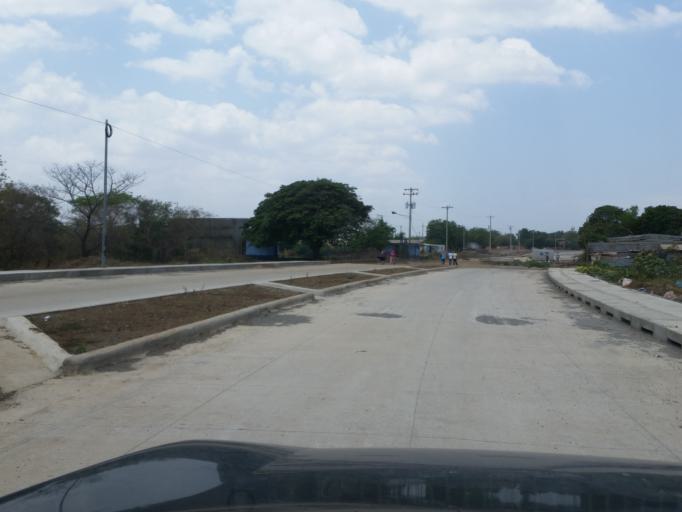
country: NI
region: Managua
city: Managua
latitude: 12.1323
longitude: -86.1861
